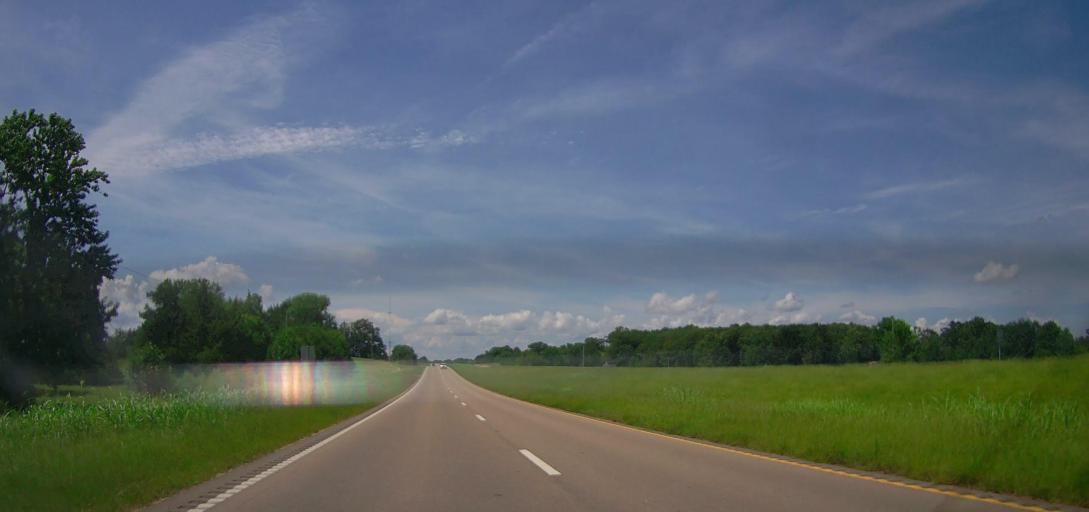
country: US
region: Mississippi
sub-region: Monroe County
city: Amory
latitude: 33.9432
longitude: -88.5997
